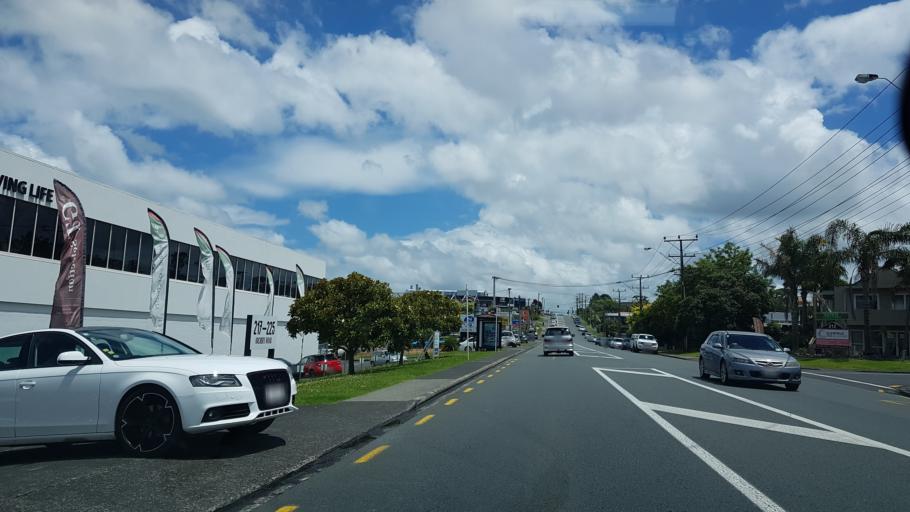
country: NZ
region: Auckland
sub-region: Auckland
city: North Shore
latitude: -36.7797
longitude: 174.7408
